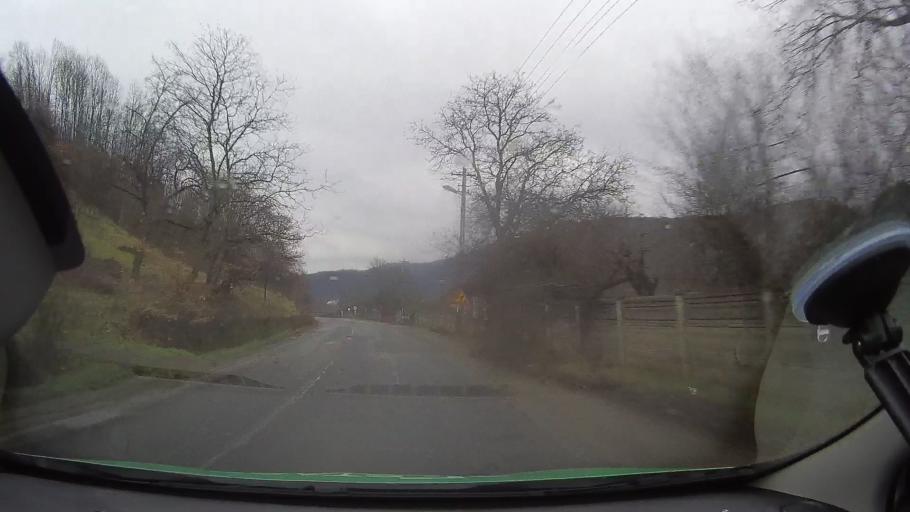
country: RO
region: Arad
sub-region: Comuna Halmagiu
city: Halmagiu
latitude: 46.2390
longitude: 22.5591
